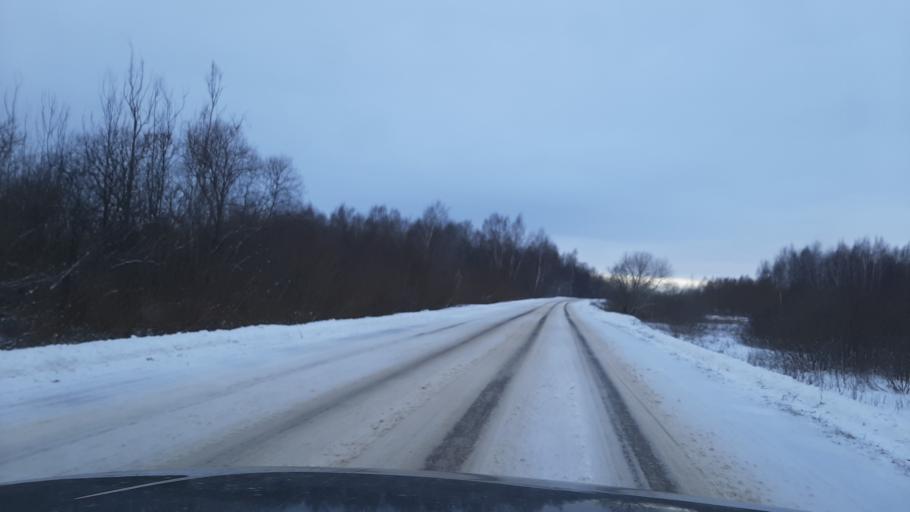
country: RU
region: Kostroma
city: Volgorechensk
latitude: 57.4413
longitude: 41.0385
